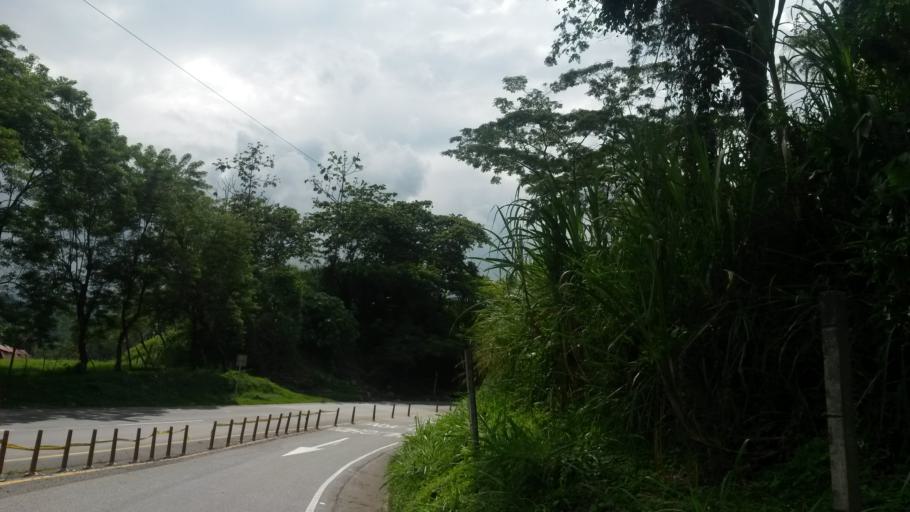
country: CO
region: Caldas
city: Chinchina
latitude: 4.9961
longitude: -75.5985
